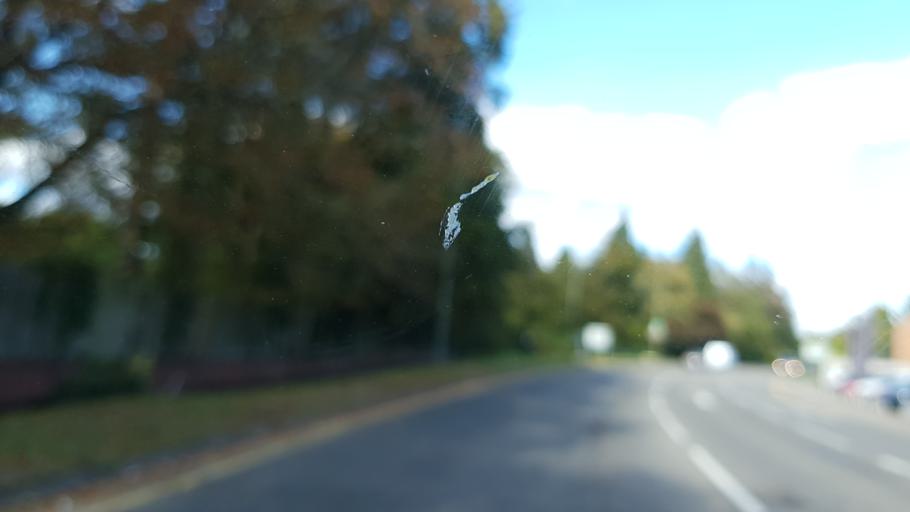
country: GB
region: England
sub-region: Surrey
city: Milford
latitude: 51.1715
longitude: -0.6521
